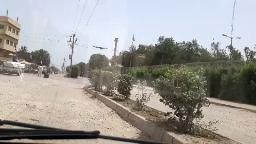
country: PK
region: Sindh
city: Malir Cantonment
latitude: 24.8399
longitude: 67.2042
